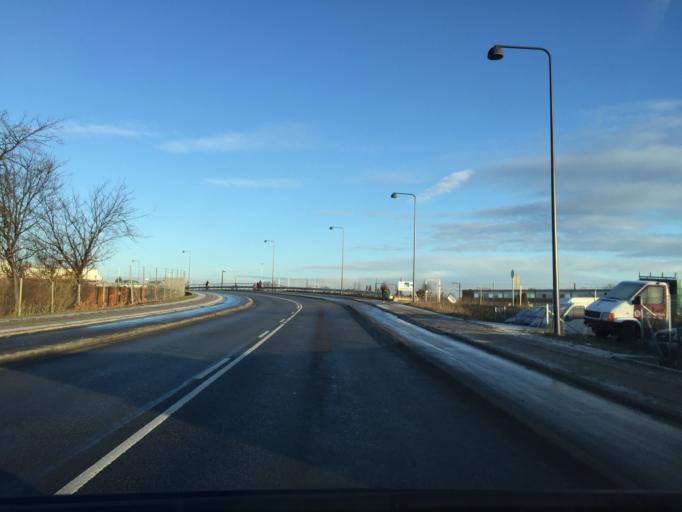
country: DK
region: Capital Region
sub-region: Hvidovre Kommune
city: Hvidovre
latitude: 55.6575
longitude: 12.5000
